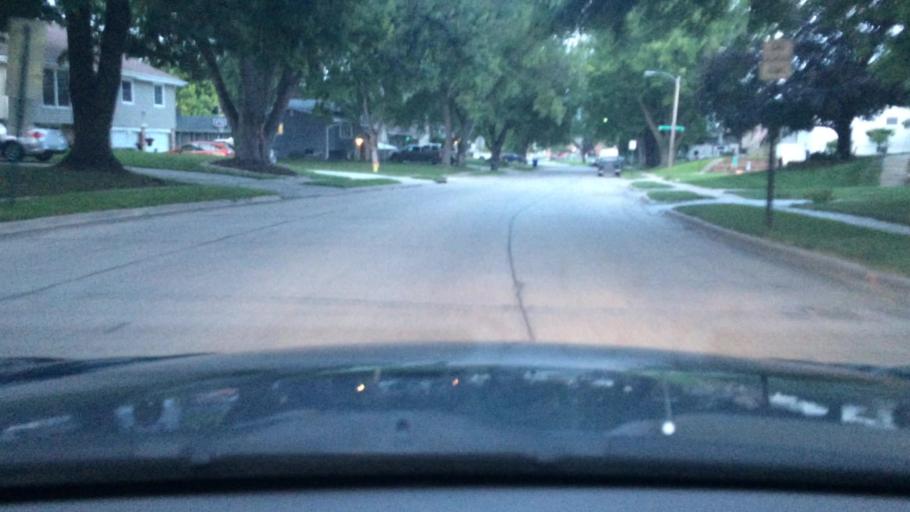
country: US
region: Nebraska
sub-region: Sarpy County
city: La Vista
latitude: 41.1849
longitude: -96.0498
